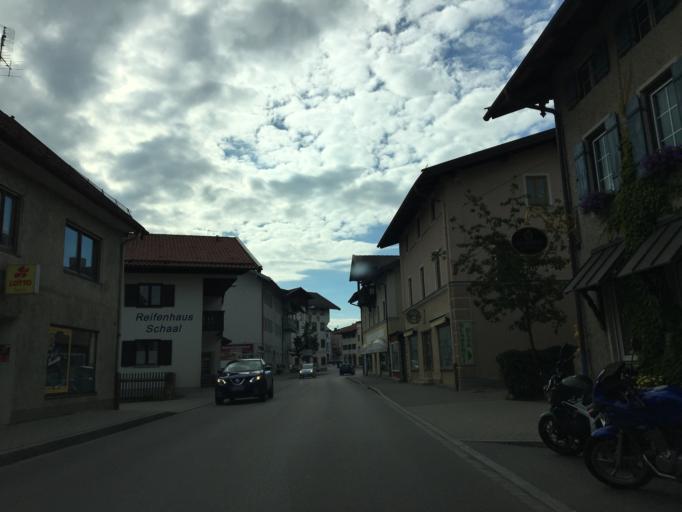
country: DE
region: Bavaria
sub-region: Upper Bavaria
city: Holzkirchen
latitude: 47.8760
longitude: 11.7032
